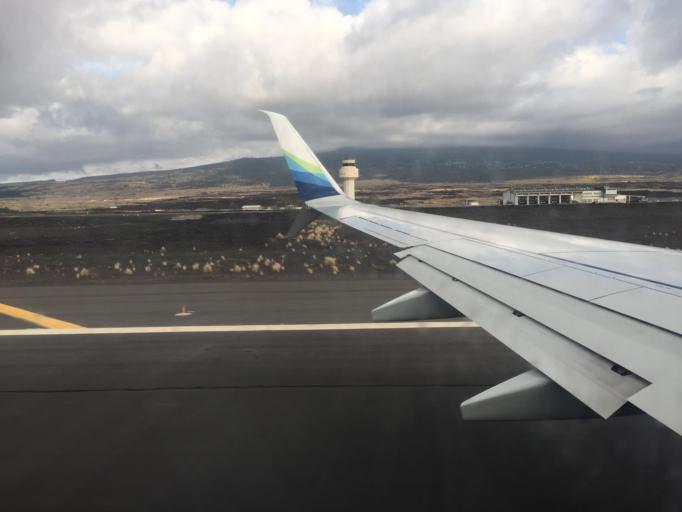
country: US
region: Hawaii
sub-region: Hawaii County
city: Kalaoa
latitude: 19.7442
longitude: -156.0452
